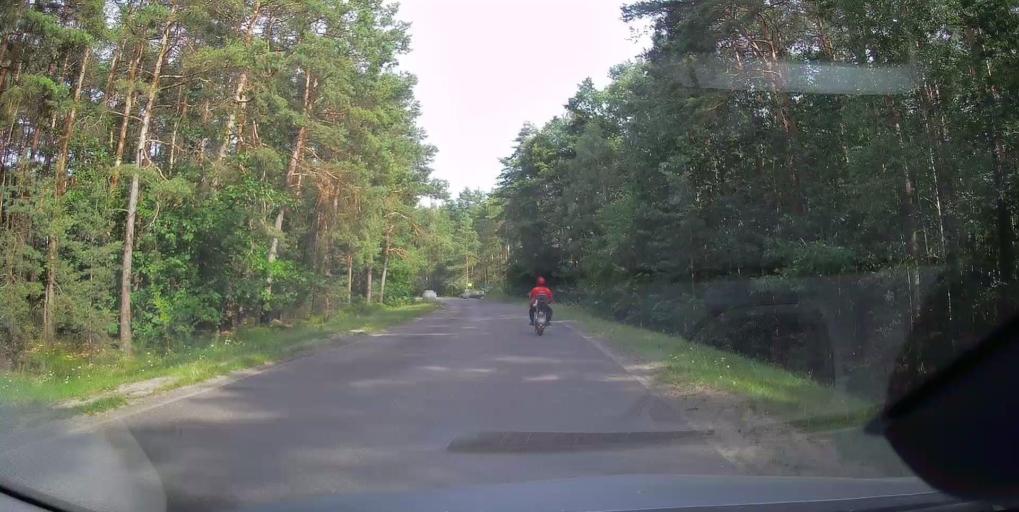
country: PL
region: Lodz Voivodeship
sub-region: Powiat tomaszowski
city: Tomaszow Mazowiecki
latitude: 51.4745
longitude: 19.9884
